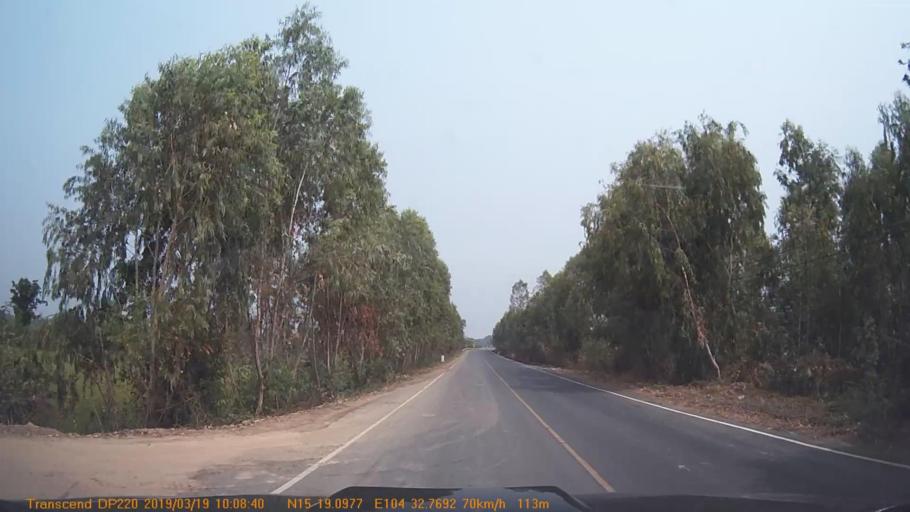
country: TH
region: Changwat Ubon Ratchathani
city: Khueang Nai
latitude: 15.3185
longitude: 104.5461
